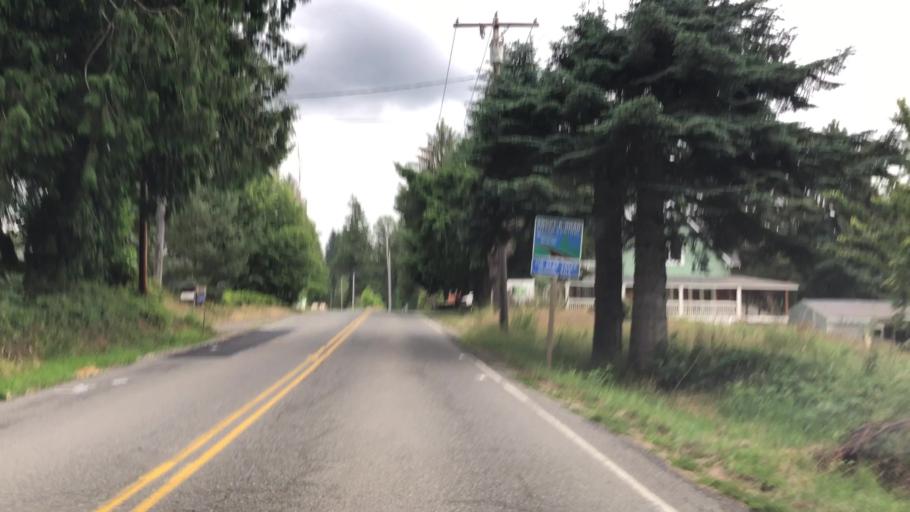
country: US
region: Washington
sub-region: King County
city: Redmond
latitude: 47.7029
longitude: -122.0909
